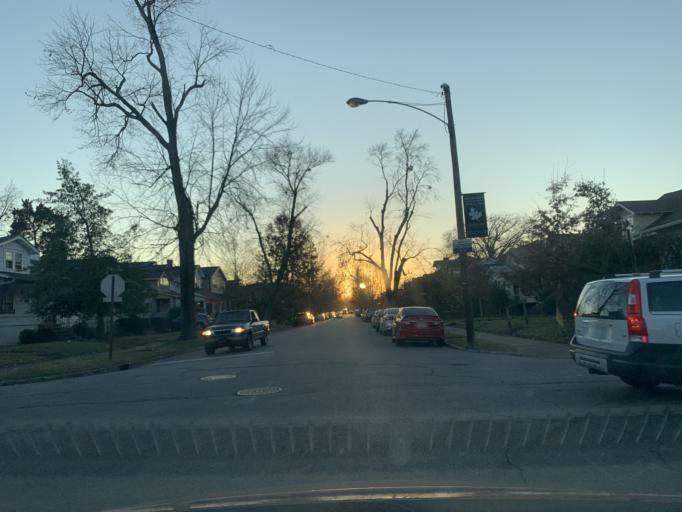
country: US
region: Kentucky
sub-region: Jefferson County
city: West Buechel
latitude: 38.2262
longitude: -85.6872
